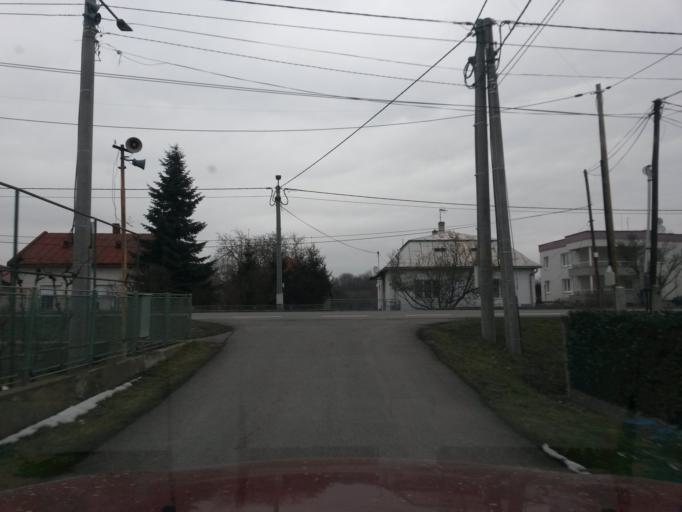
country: SK
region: Kosicky
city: Michalovce
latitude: 48.7273
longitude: 21.8631
